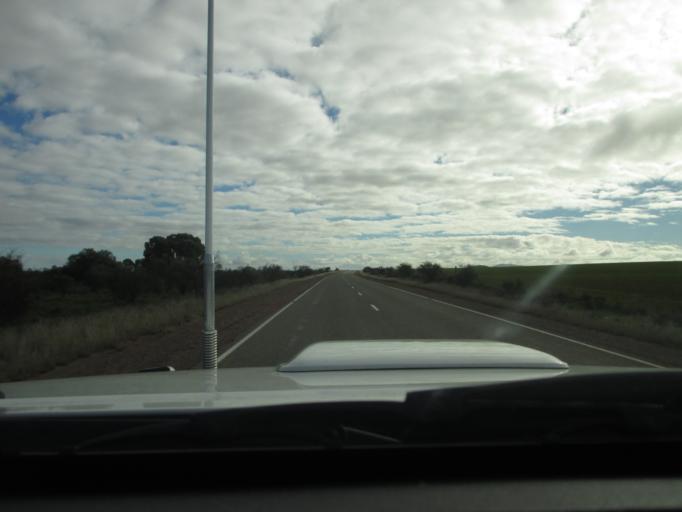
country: AU
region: South Australia
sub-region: Flinders Ranges
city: Quorn
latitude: -32.4532
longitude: 138.5369
